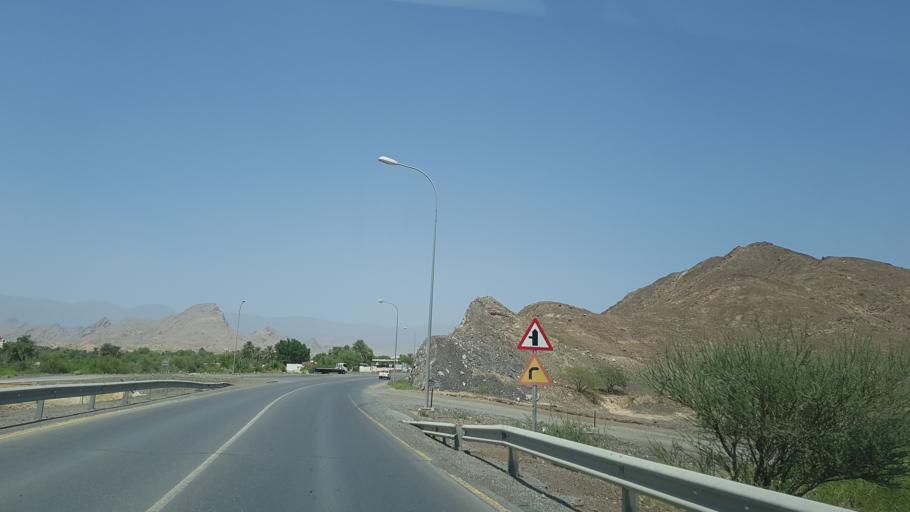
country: OM
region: Muhafazat ad Dakhiliyah
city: Bahla'
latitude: 22.9740
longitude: 57.3035
